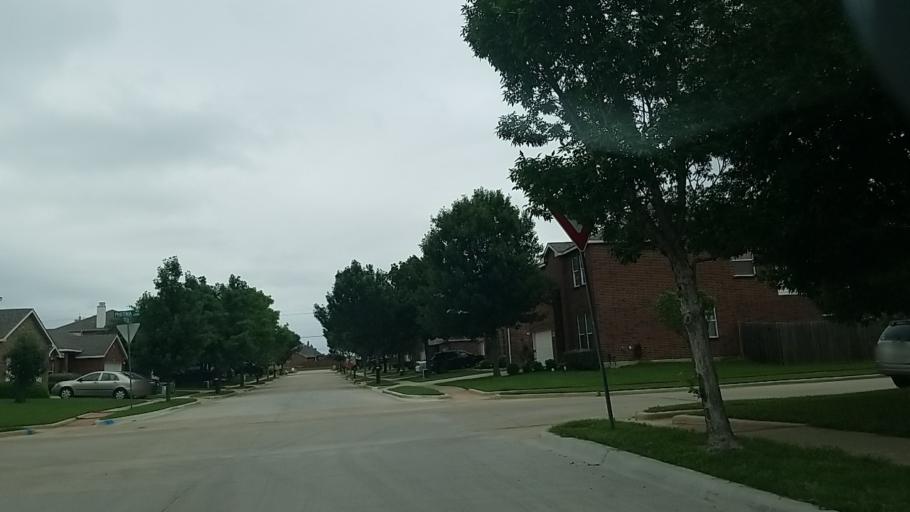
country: US
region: Texas
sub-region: Denton County
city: Corinth
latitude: 33.1694
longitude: -97.0732
